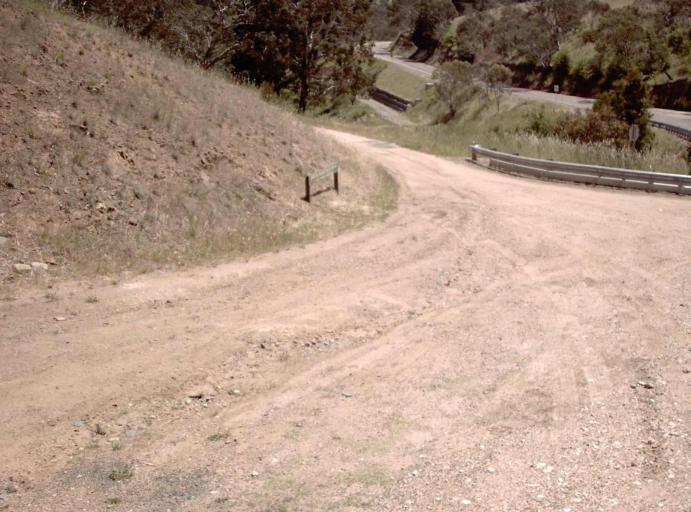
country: AU
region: Victoria
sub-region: Alpine
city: Mount Beauty
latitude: -37.1122
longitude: 147.5777
